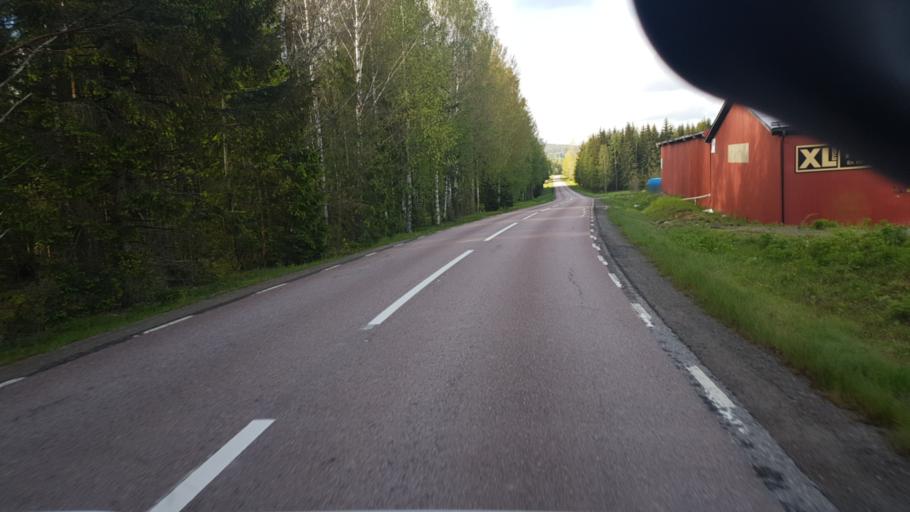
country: SE
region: Vaermland
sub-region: Eda Kommun
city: Amotfors
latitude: 59.7455
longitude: 12.2107
